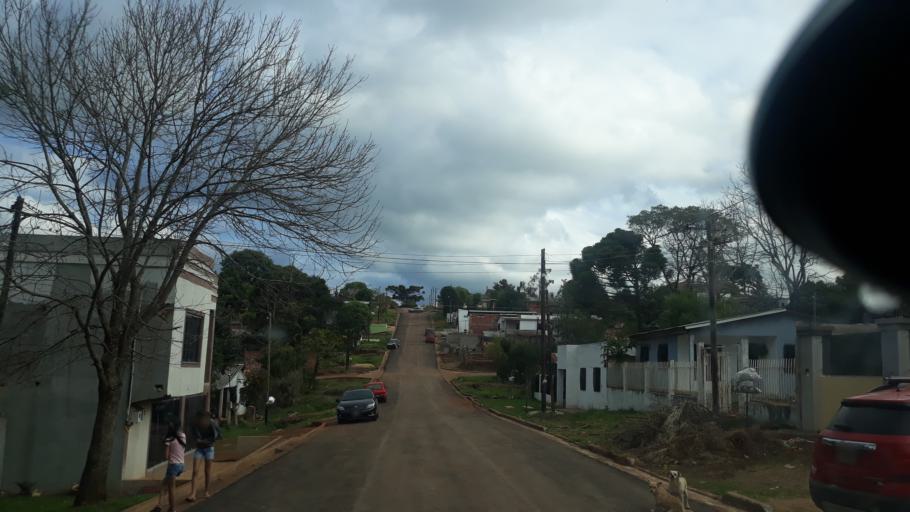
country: AR
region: Misiones
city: Bernardo de Irigoyen
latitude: -26.2637
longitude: -53.6462
